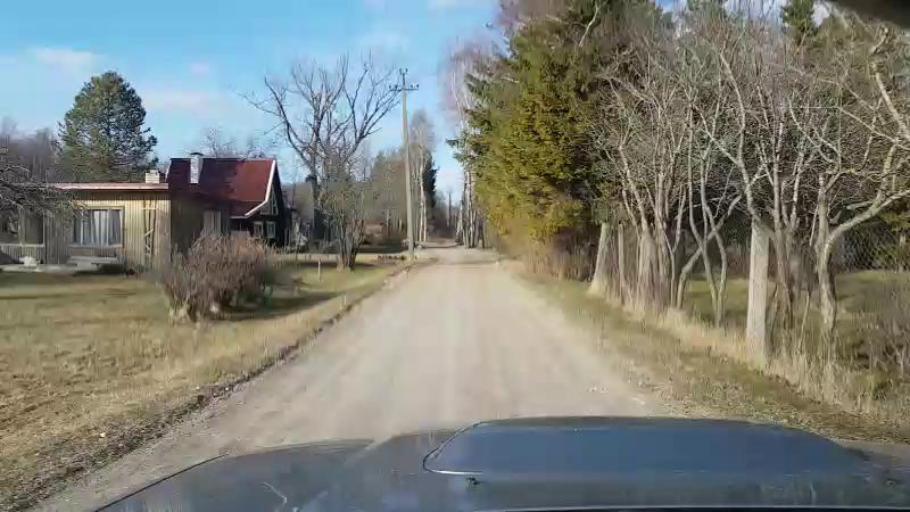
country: EE
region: Jaervamaa
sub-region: Paide linn
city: Paide
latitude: 58.8882
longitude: 25.5307
